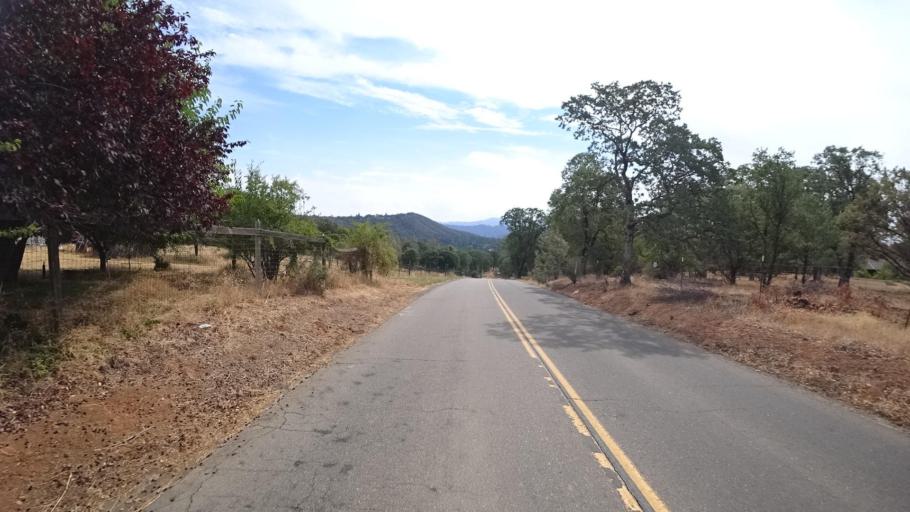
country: US
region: California
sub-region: Mariposa County
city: Midpines
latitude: 37.5340
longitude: -119.9637
